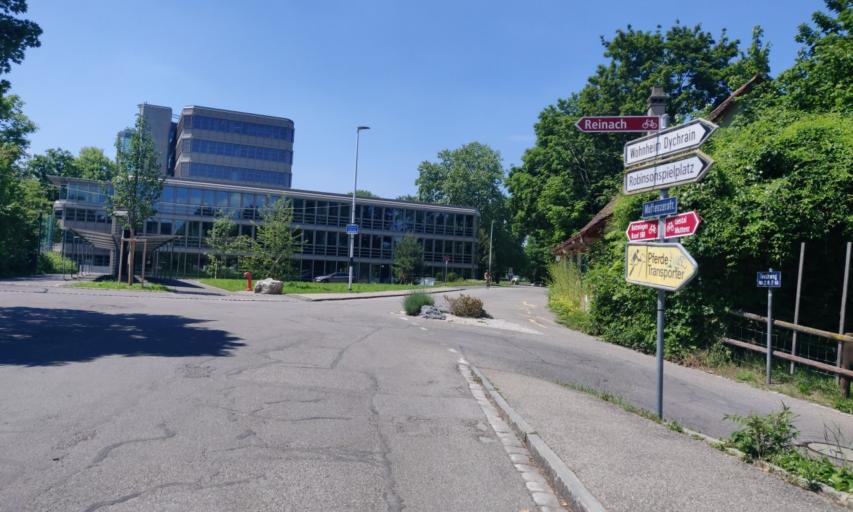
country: CH
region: Basel-Landschaft
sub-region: Bezirk Arlesheim
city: Munchenstein
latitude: 47.5274
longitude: 7.6186
